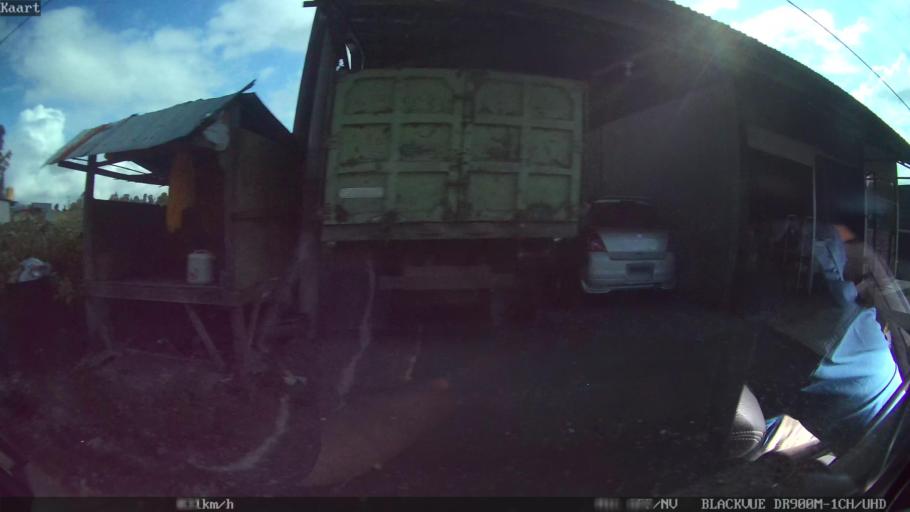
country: ID
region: Bali
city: Banjar Trunyan
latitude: -8.2184
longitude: 115.3930
